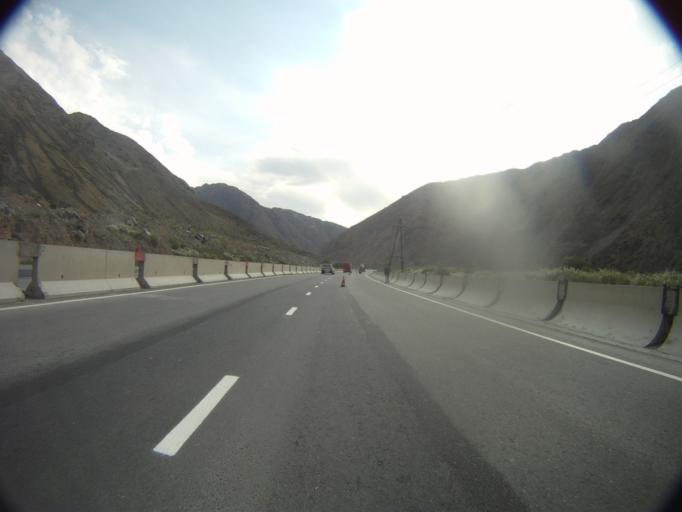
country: KG
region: Chuy
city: Bystrovka
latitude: 42.5857
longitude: 75.8098
